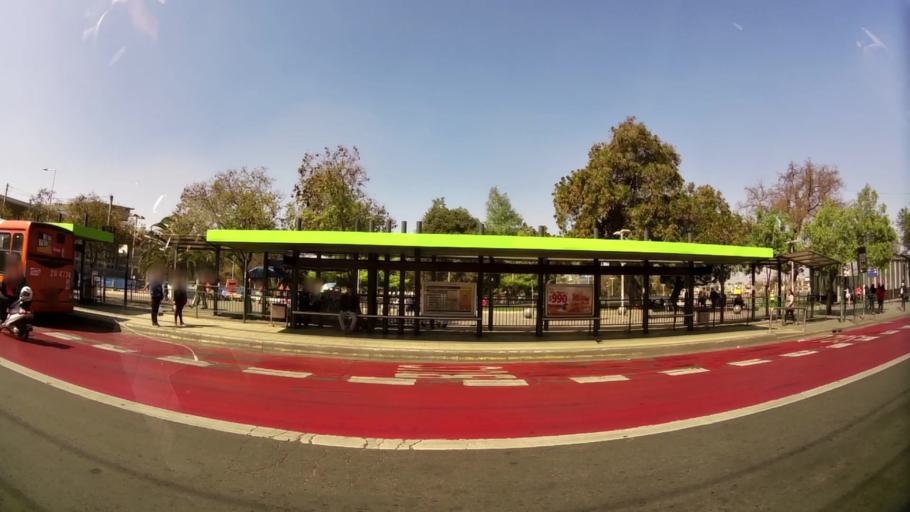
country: CL
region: Santiago Metropolitan
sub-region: Provincia de Santiago
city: Lo Prado
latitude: -33.5094
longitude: -70.7572
